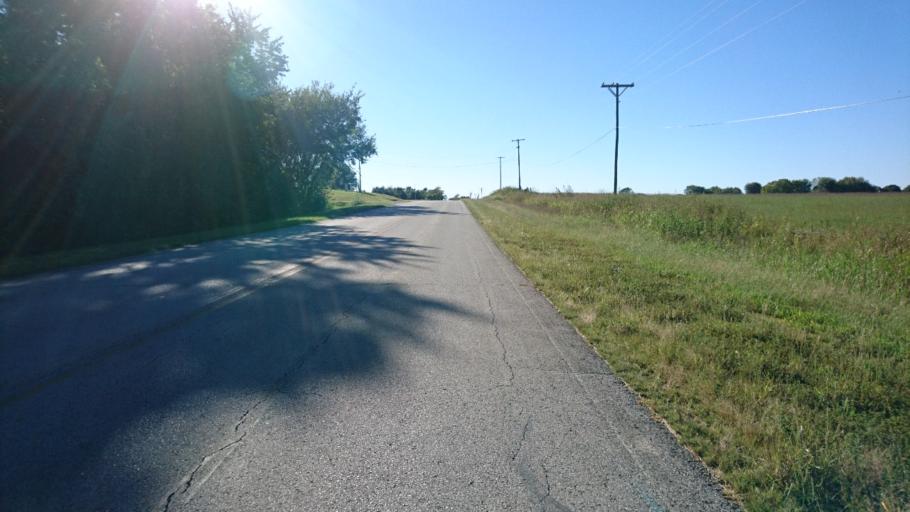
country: US
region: Missouri
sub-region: Jasper County
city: Carthage
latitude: 37.1732
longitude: -94.3593
